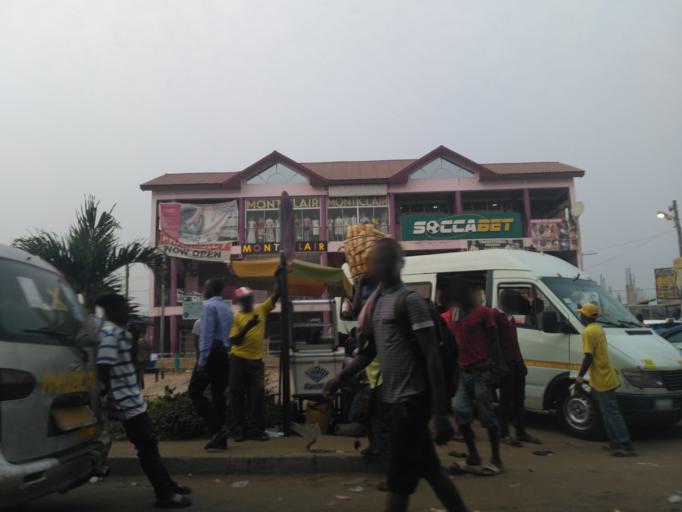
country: GH
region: Greater Accra
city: Dome
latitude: 5.6579
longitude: -0.2659
